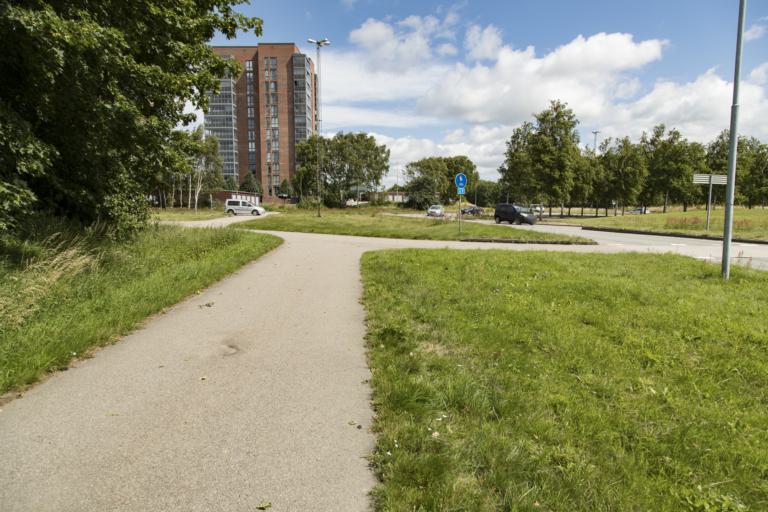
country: SE
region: Halland
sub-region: Varbergs Kommun
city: Varberg
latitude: 57.0899
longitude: 12.2635
